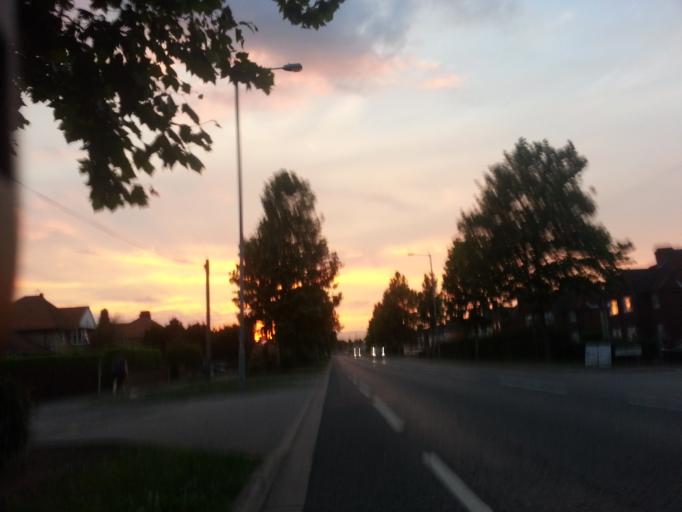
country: GB
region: England
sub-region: Suffolk
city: Ipswich
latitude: 52.0339
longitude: 1.1959
